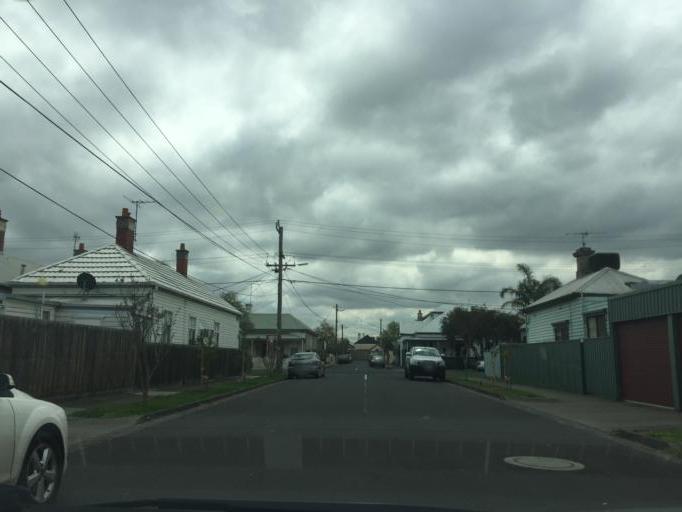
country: AU
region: Victoria
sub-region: Maribyrnong
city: Seddon
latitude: -37.8106
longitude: 144.8888
